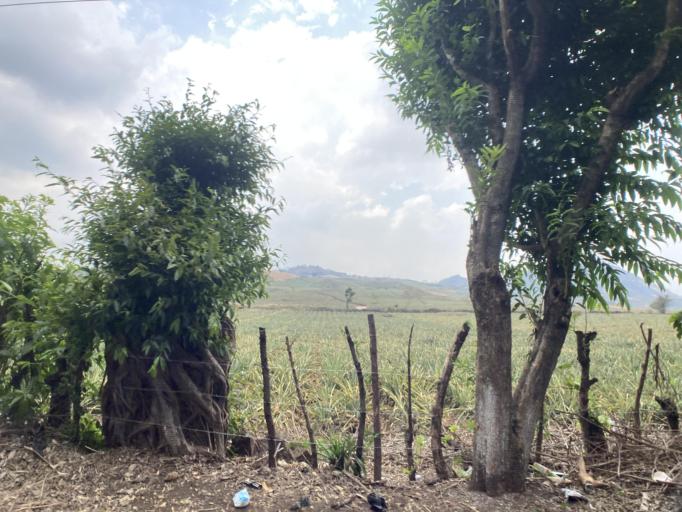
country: GT
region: Guatemala
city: Fraijanes
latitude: 14.3742
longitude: -90.4904
